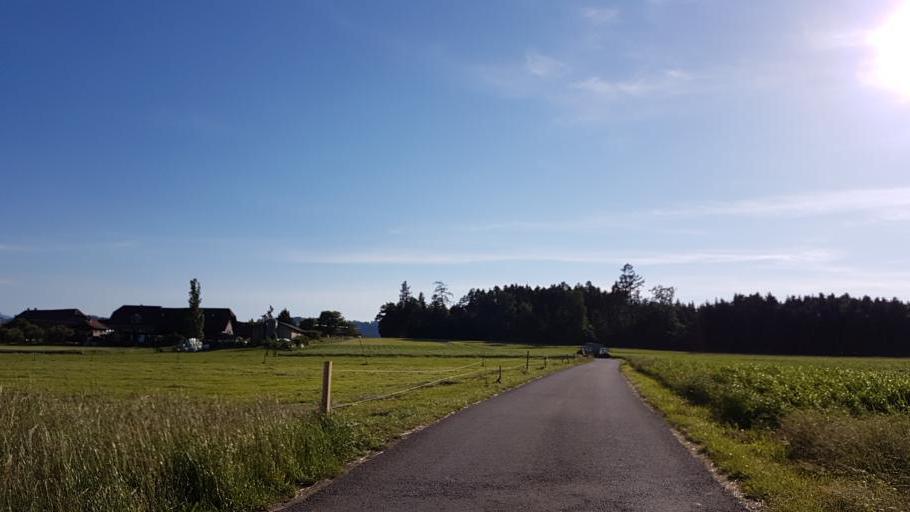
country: CH
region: Bern
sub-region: Bern-Mittelland District
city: Rubigen
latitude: 46.9036
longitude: 7.5640
